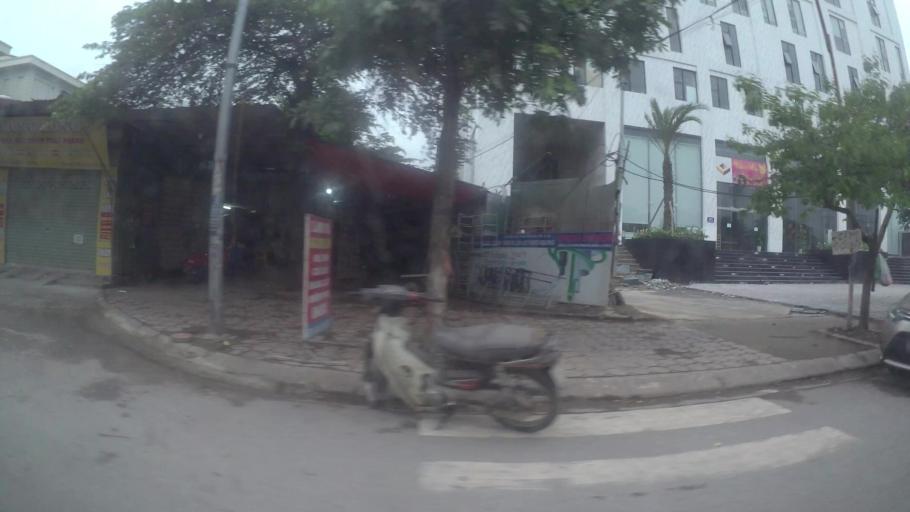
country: VN
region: Ha Noi
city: Cau Dien
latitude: 21.0344
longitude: 105.7822
